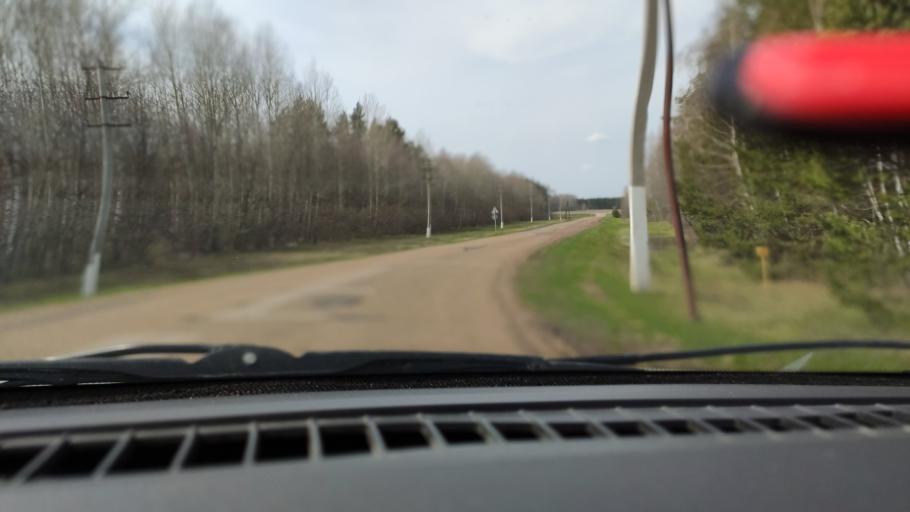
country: RU
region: Bashkortostan
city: Dyurtyuli
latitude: 55.2839
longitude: 55.0621
